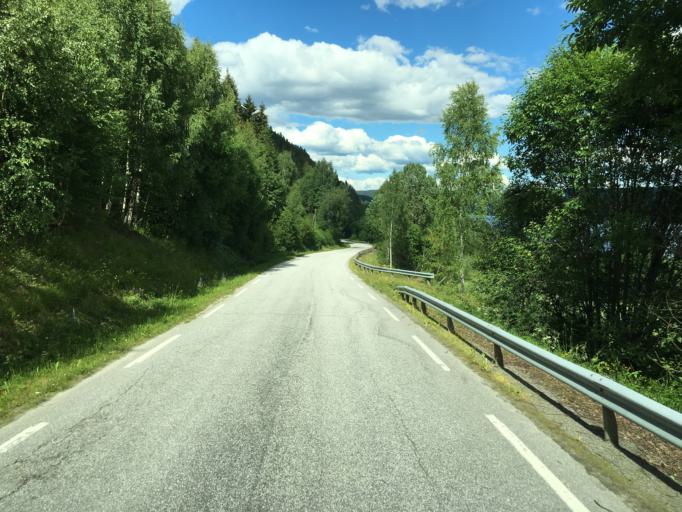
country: NO
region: Oppland
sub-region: Sondre Land
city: Hov
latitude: 60.5750
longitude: 10.2889
